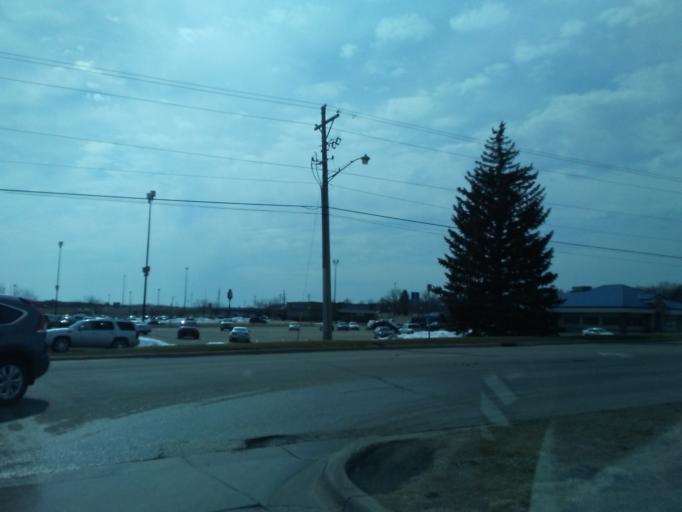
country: US
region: Minnesota
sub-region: Olmsted County
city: Rochester
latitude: 43.9811
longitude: -92.4600
